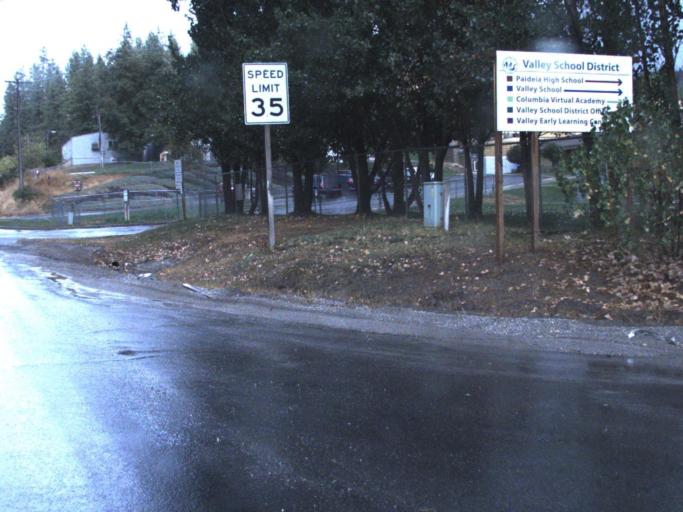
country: US
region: Washington
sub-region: Stevens County
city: Chewelah
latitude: 48.1687
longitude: -117.7227
